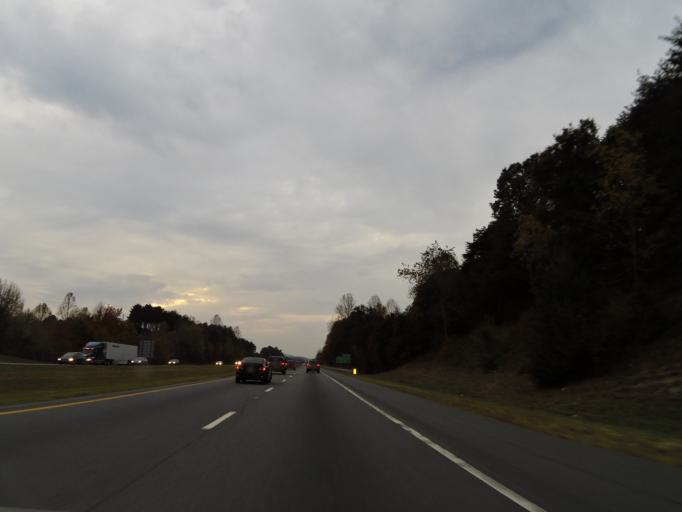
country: US
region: North Carolina
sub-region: Catawba County
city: Longview
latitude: 35.7067
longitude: -81.3786
